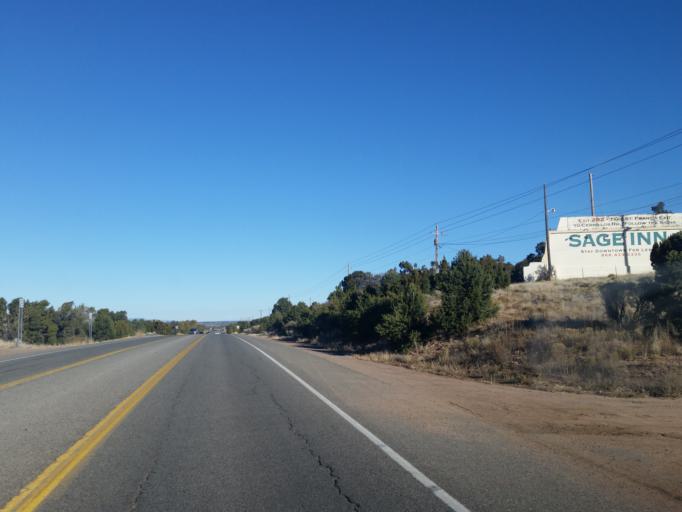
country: US
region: New Mexico
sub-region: Santa Fe County
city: Santa Fe
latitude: 35.6290
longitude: -105.9225
